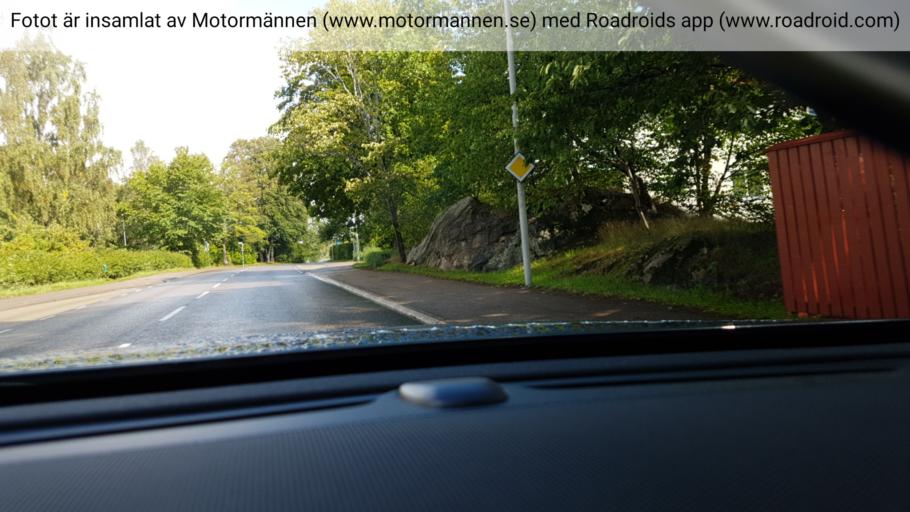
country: SE
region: Vaestra Goetaland
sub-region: Vanersborgs Kommun
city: Vanersborg
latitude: 58.3726
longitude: 12.2858
